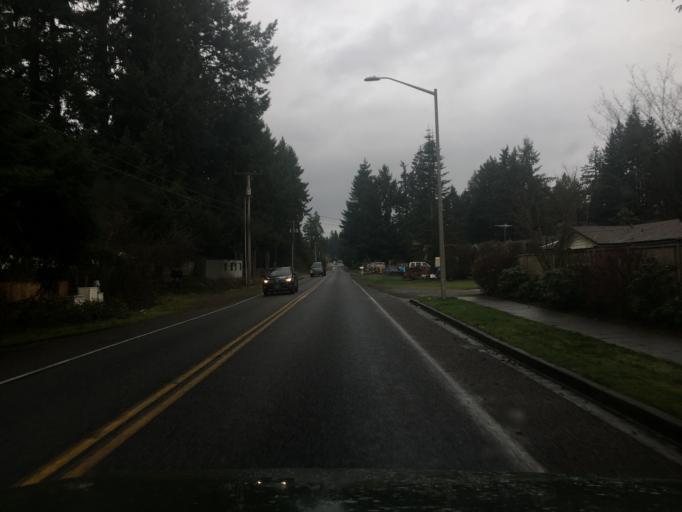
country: US
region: Washington
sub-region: Thurston County
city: Tanglewilde-Thompson Place
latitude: 47.0466
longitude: -122.7913
